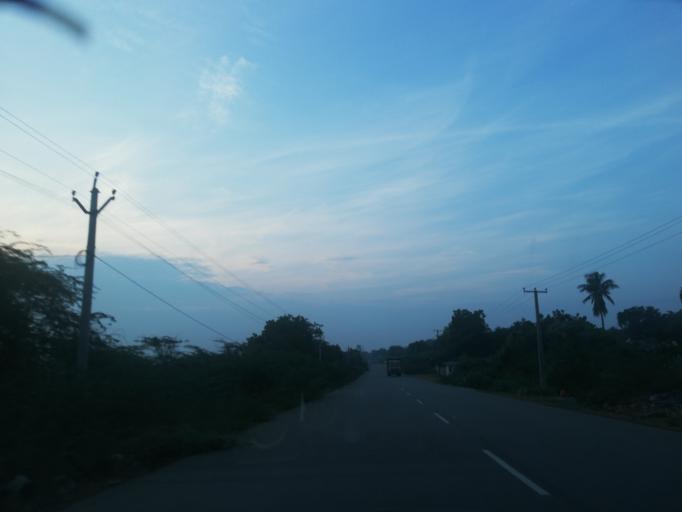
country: IN
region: Andhra Pradesh
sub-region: Guntur
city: Macherla
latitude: 16.5906
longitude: 79.3177
